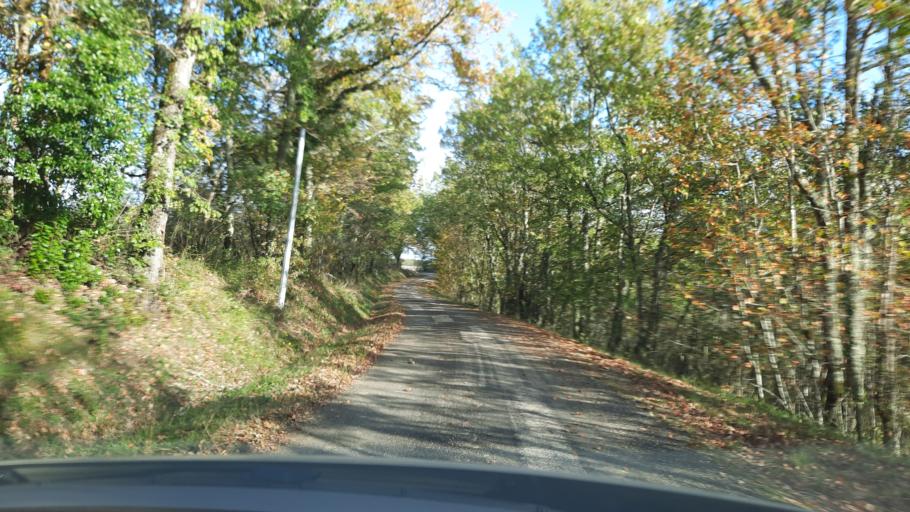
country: FR
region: Midi-Pyrenees
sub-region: Departement du Tarn-et-Garonne
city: Lafrancaise
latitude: 44.1768
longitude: 1.2874
